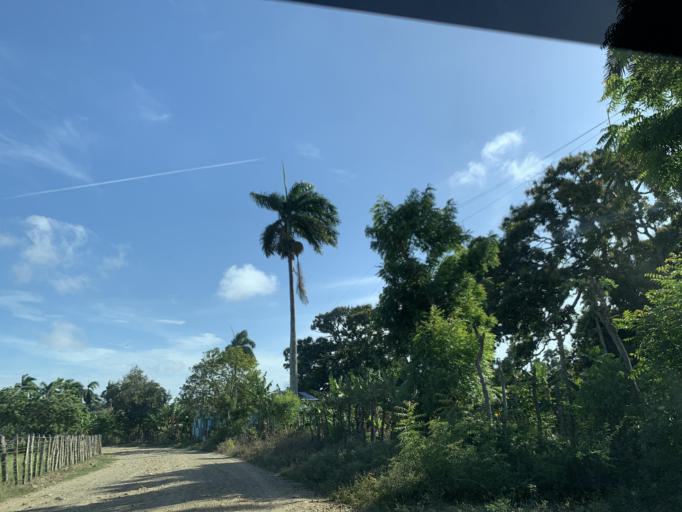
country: DO
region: Puerto Plata
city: Luperon
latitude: 19.8930
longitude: -70.8838
